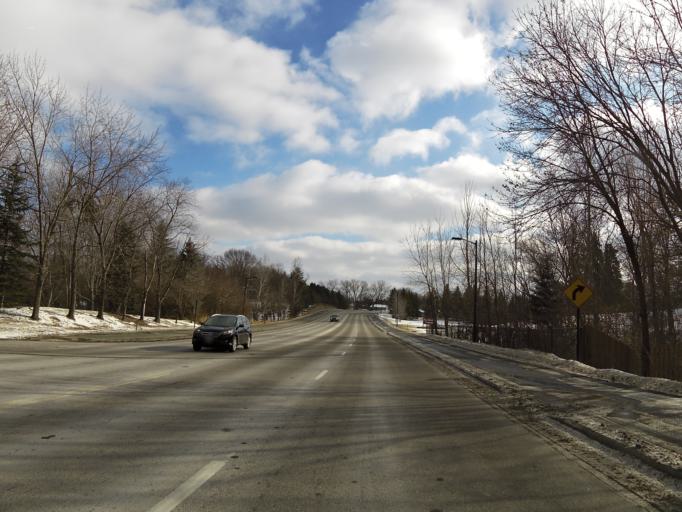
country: US
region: Minnesota
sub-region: Hennepin County
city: Eden Prairie
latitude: 44.8445
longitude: -93.4823
